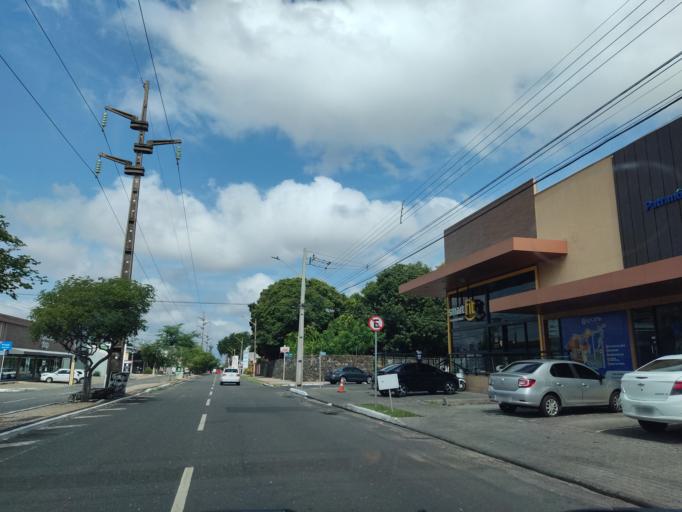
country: BR
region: Piaui
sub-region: Teresina
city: Teresina
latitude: -5.0700
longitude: -42.7855
